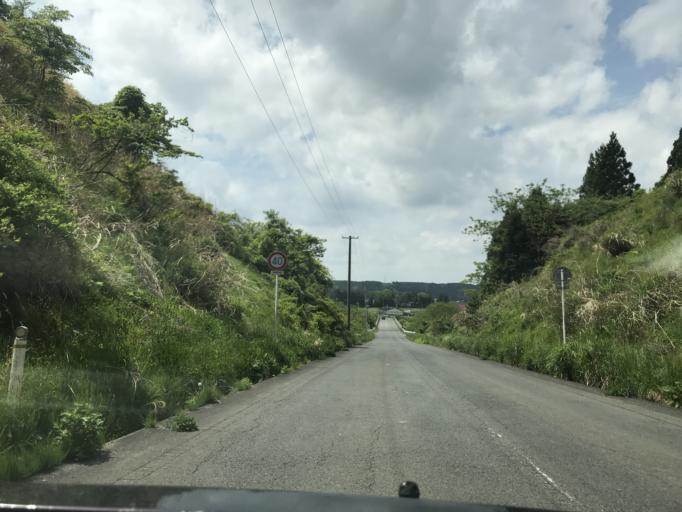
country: JP
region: Miyagi
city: Furukawa
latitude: 38.7545
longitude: 140.9388
